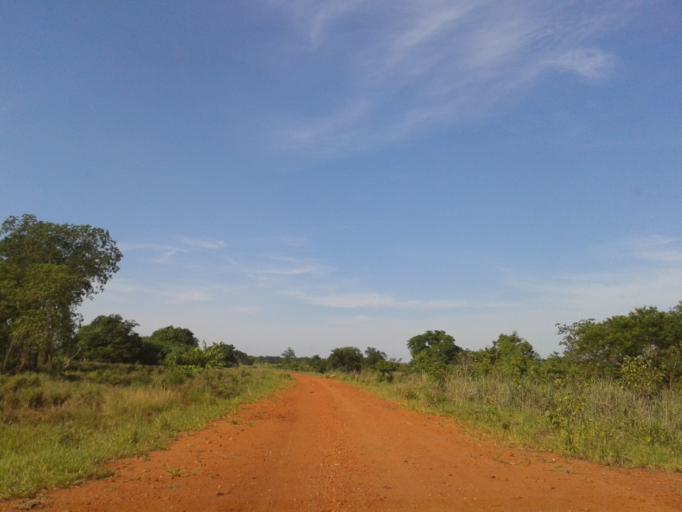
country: BR
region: Minas Gerais
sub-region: Santa Vitoria
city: Santa Vitoria
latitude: -19.1184
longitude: -50.5550
